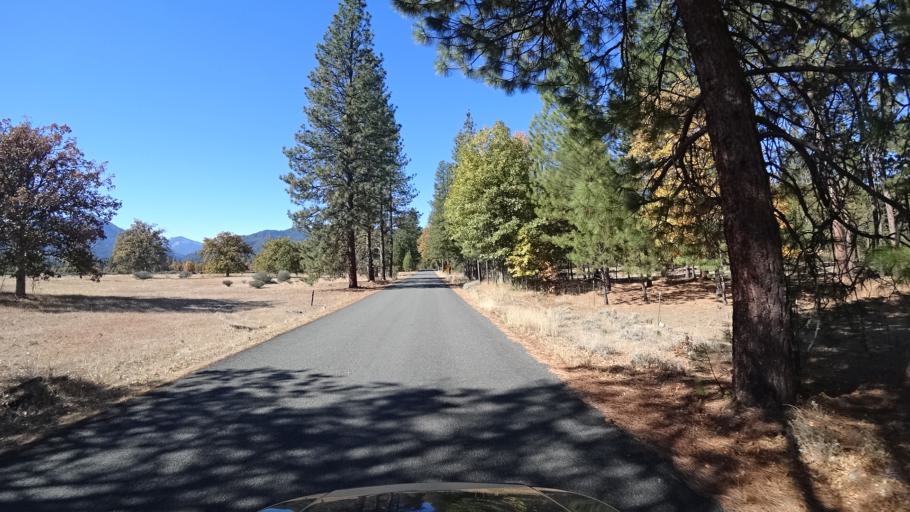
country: US
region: California
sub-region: Siskiyou County
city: Yreka
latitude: 41.5485
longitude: -122.9312
